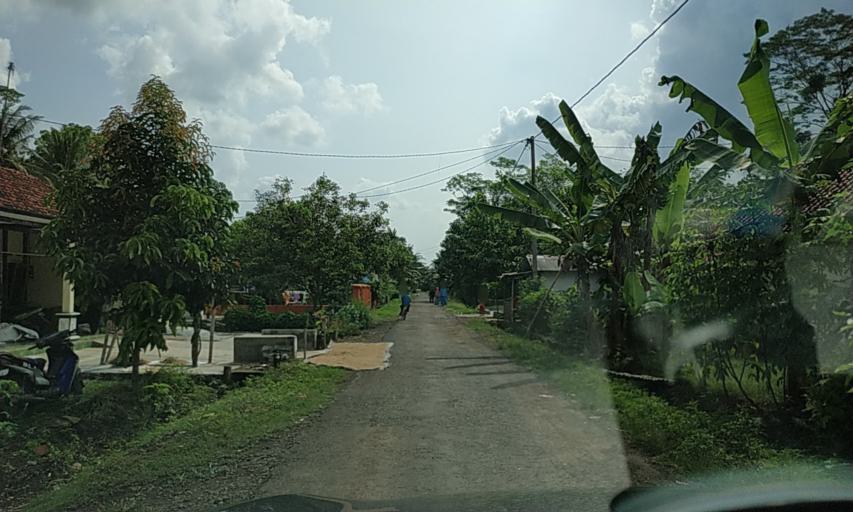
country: ID
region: Central Java
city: Bakung
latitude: -7.3498
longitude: 108.6624
